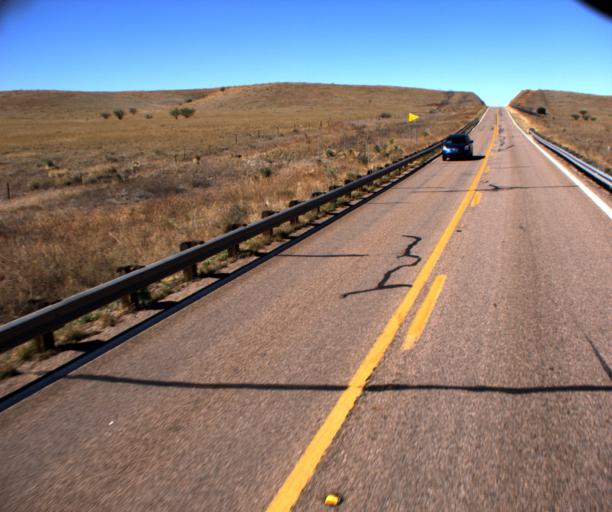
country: US
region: Arizona
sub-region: Cochise County
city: Huachuca City
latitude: 31.7089
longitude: -110.5767
